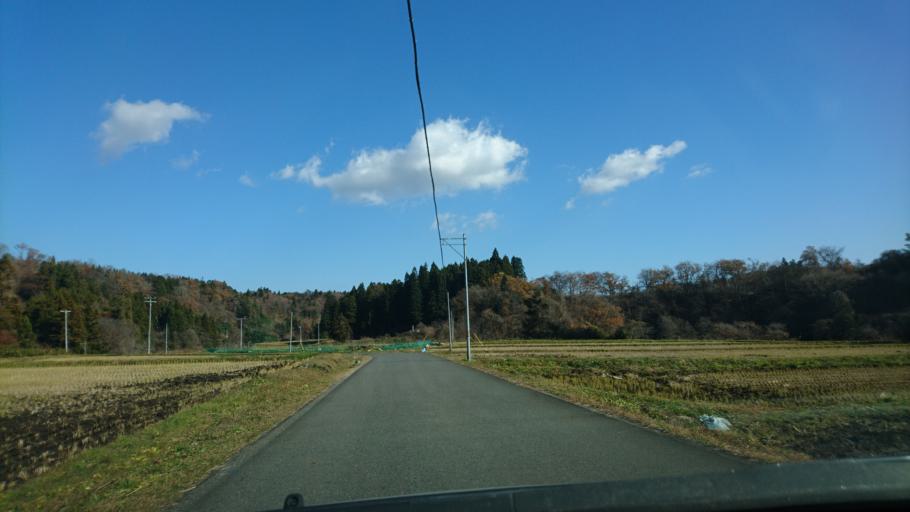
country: JP
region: Iwate
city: Ichinoseki
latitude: 38.9972
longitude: 141.0681
